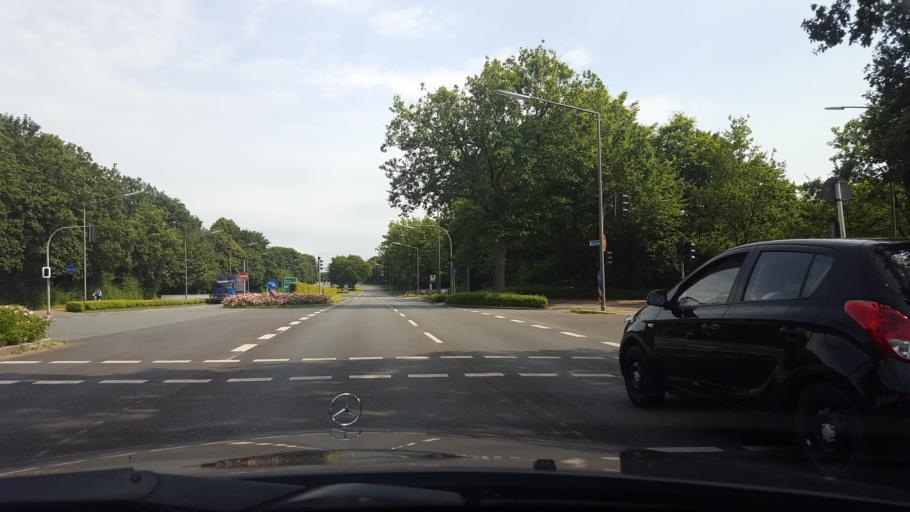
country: DE
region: North Rhine-Westphalia
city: Marl
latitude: 51.6510
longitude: 7.0978
